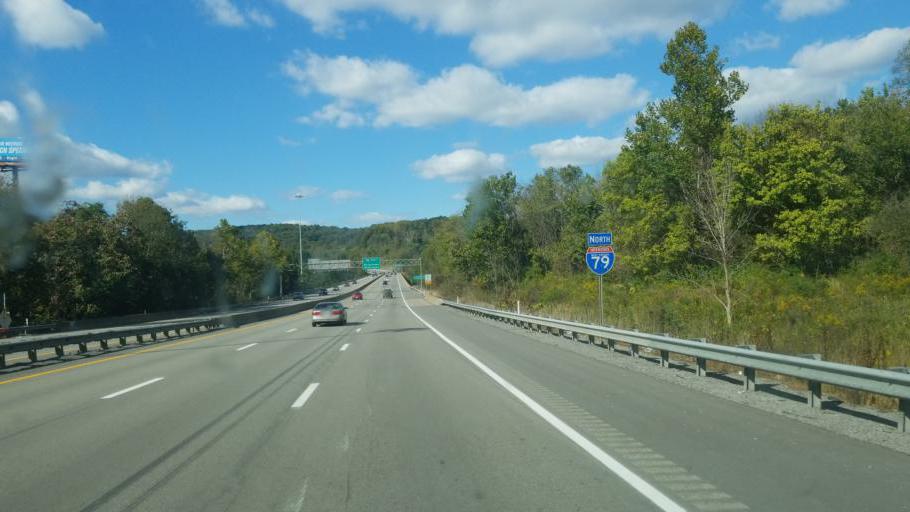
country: US
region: West Virginia
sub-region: Monongalia County
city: Morgantown
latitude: 39.5838
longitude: -79.9792
